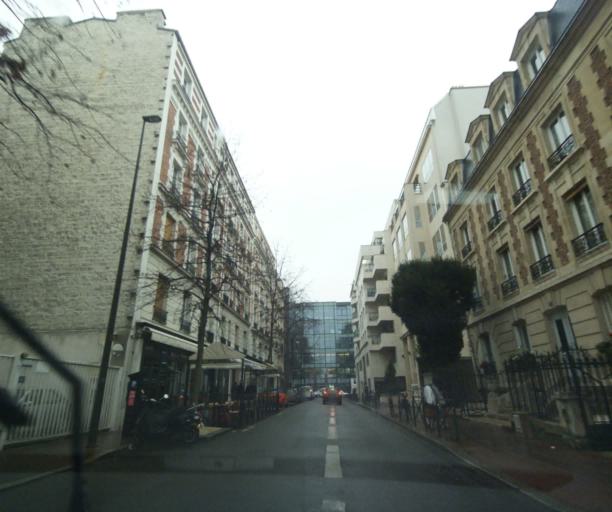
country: FR
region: Ile-de-France
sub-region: Departement des Hauts-de-Seine
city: Levallois-Perret
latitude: 48.8896
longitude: 2.2817
